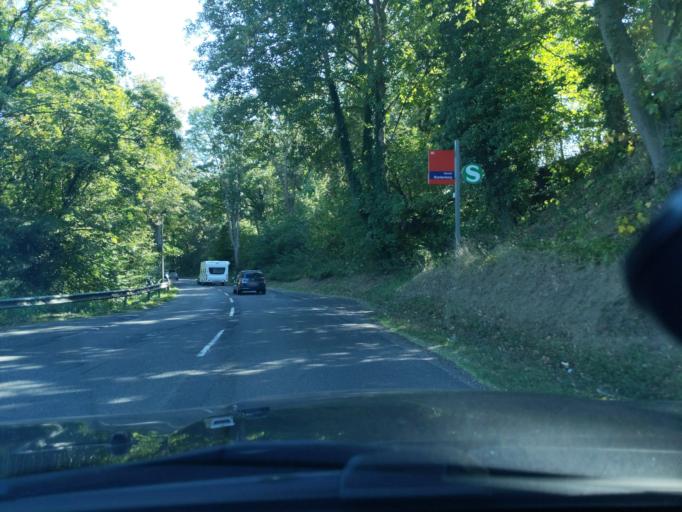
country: DE
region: North Rhine-Westphalia
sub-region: Regierungsbezirk Koln
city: Hennef
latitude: 50.7674
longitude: 7.3484
